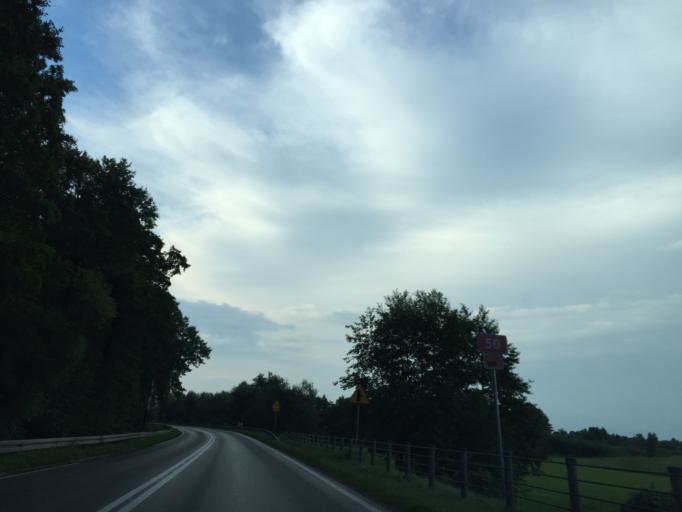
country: PL
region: Masovian Voivodeship
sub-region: Powiat ostrowski
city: Brok
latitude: 52.6885
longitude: 21.8522
